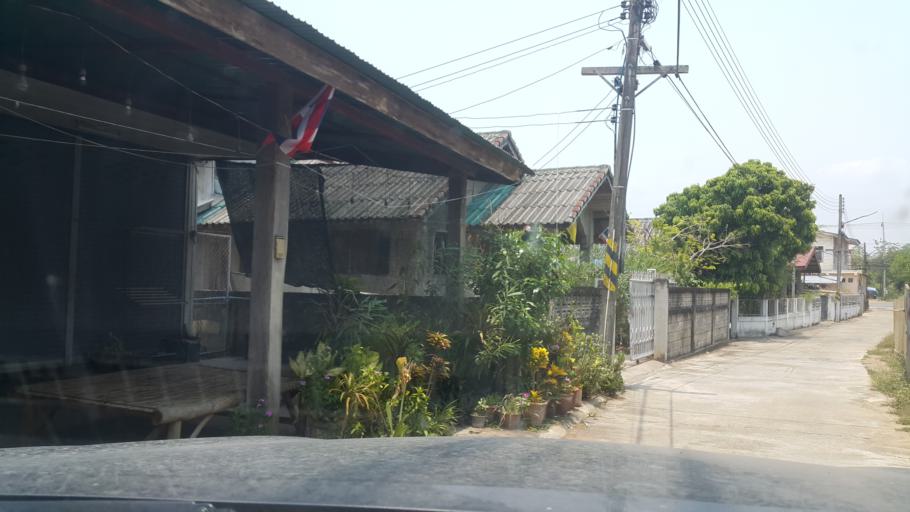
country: TH
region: Lampang
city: Thoen
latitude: 17.6374
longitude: 99.2365
